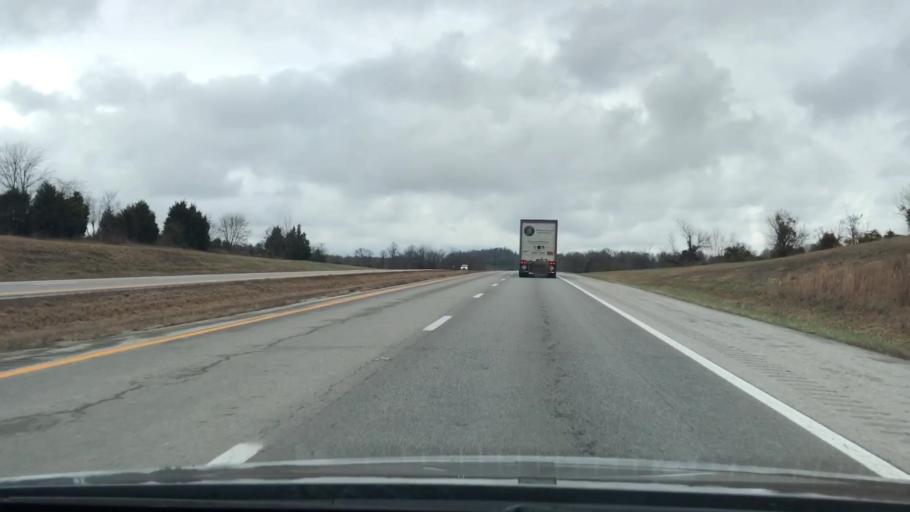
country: US
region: Kentucky
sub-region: Christian County
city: Hopkinsville
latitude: 36.9245
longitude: -87.4721
